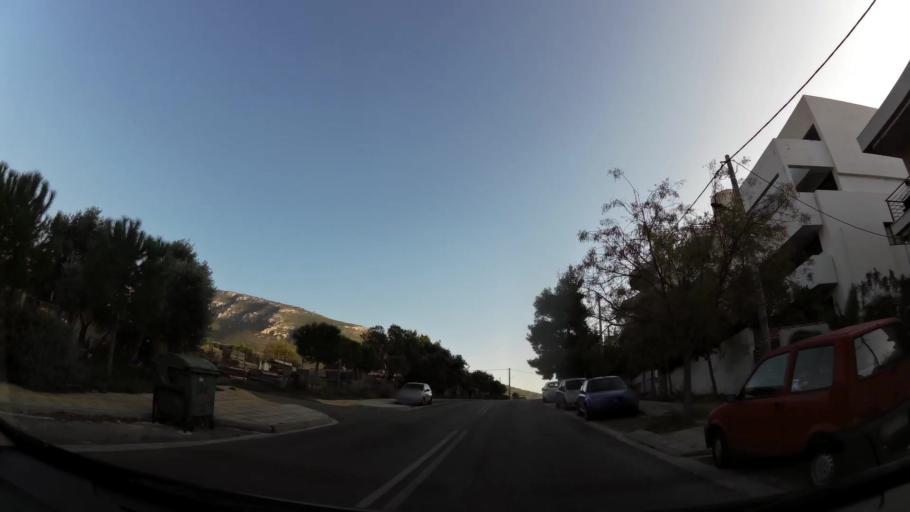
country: GR
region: Attica
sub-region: Nomarchia Athinas
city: Argyroupoli
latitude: 37.8922
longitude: 23.7768
